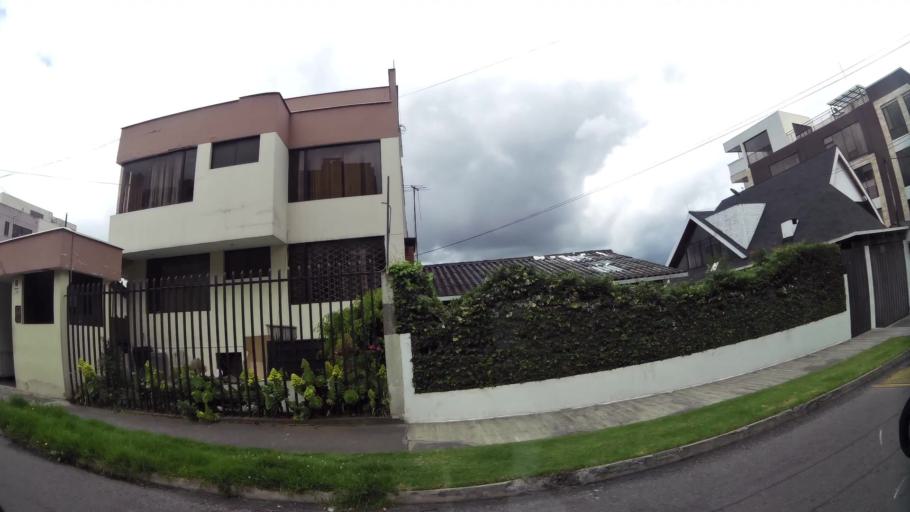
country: EC
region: Pichincha
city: Quito
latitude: -0.1672
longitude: -78.4948
